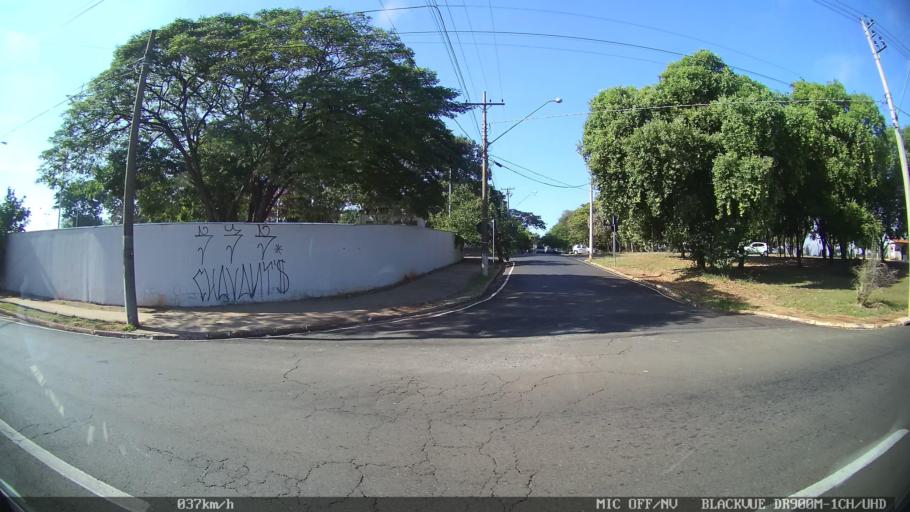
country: BR
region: Sao Paulo
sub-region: Sao Jose Do Rio Preto
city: Sao Jose do Rio Preto
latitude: -20.8134
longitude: -49.4073
